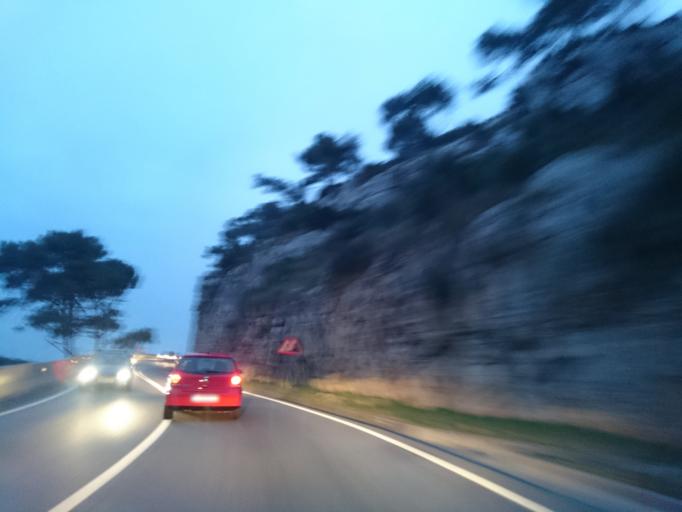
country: ES
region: Catalonia
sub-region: Provincia de Barcelona
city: Sitges
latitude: 41.2515
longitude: 1.8885
